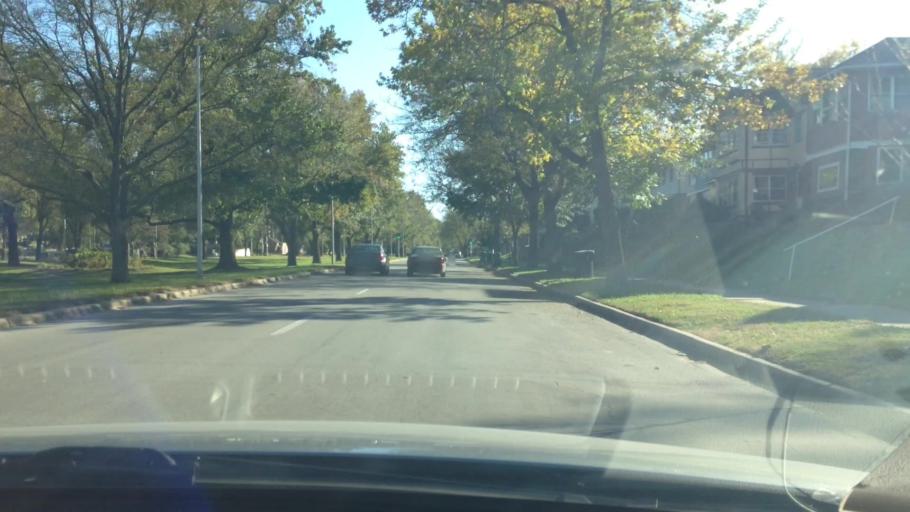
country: US
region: Kansas
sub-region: Johnson County
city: Mission Hills
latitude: 39.0285
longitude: -94.5679
